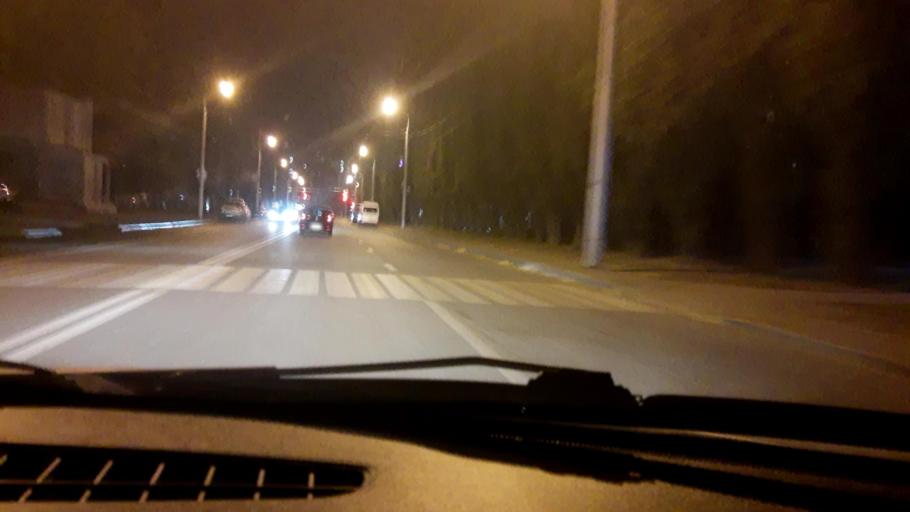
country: RU
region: Bashkortostan
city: Ufa
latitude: 54.7659
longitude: 56.0683
